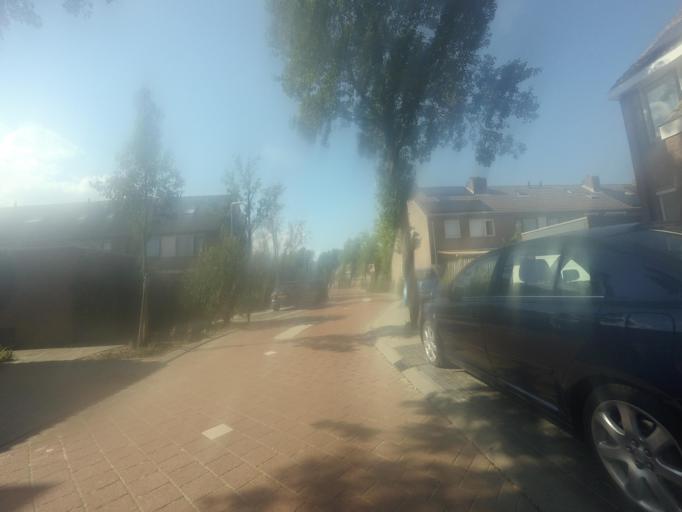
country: NL
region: North Brabant
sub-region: Gemeente Goirle
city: Goirle
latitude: 51.5257
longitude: 5.0545
